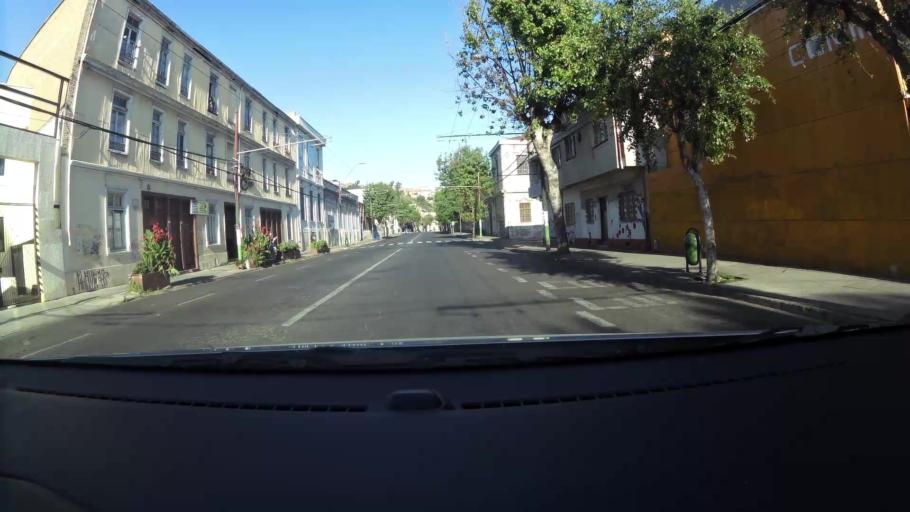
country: CL
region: Valparaiso
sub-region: Provincia de Valparaiso
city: Valparaiso
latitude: -33.0494
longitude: -71.6147
